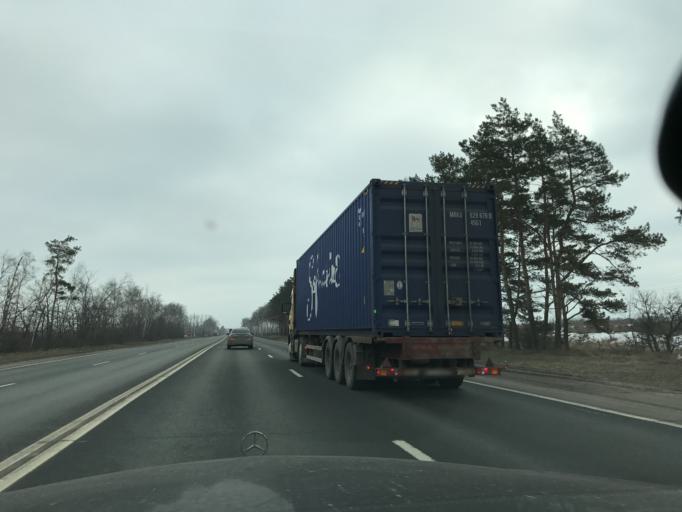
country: RU
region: Vladimir
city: Vorsha
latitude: 56.0419
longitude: 40.0541
